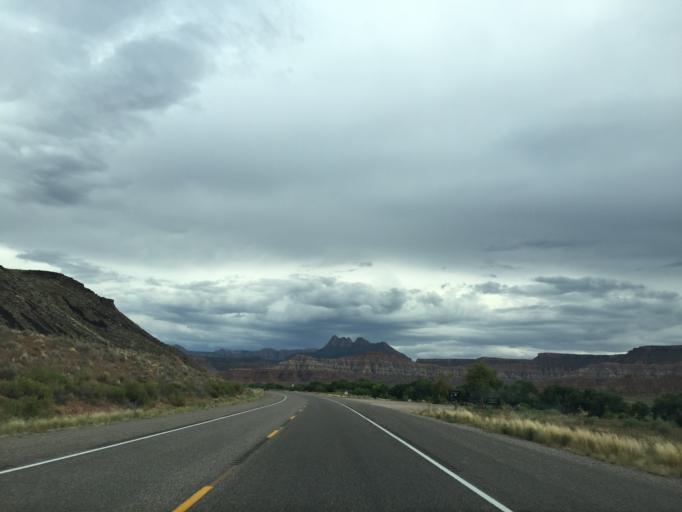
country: US
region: Utah
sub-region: Washington County
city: LaVerkin
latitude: 37.1905
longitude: -113.1426
